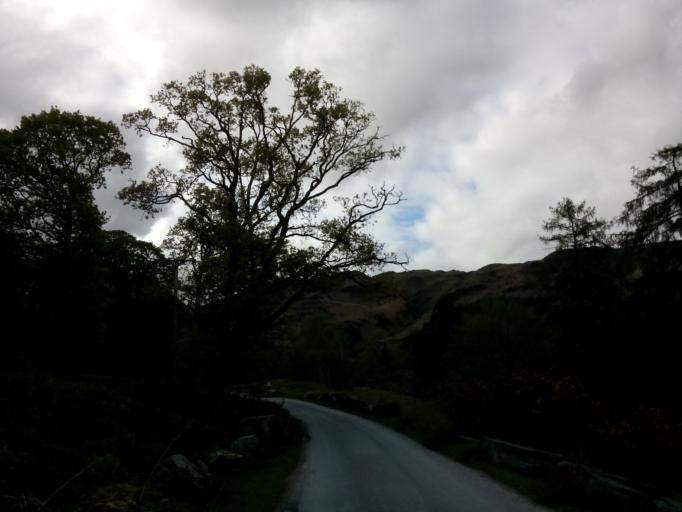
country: GB
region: England
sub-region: Cumbria
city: Ambleside
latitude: 54.4345
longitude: -3.0404
